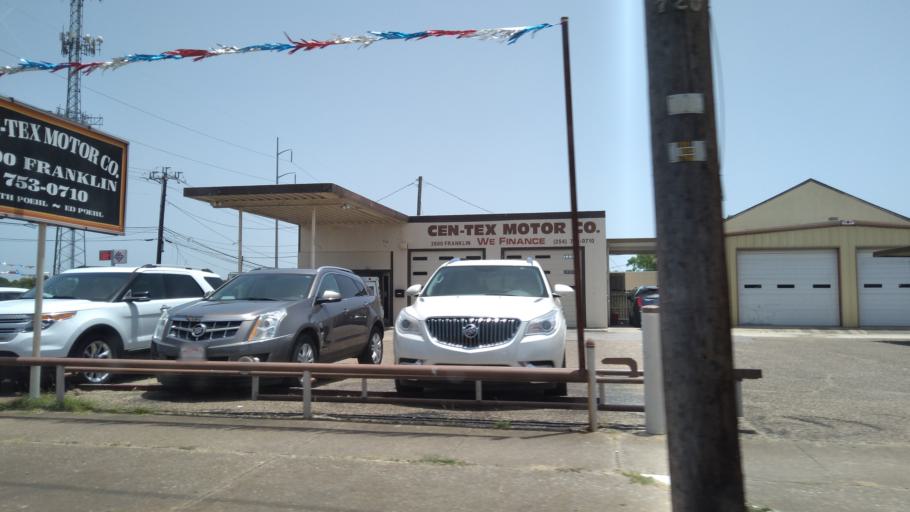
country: US
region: Texas
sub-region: McLennan County
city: Waco
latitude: 31.5386
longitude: -97.1504
